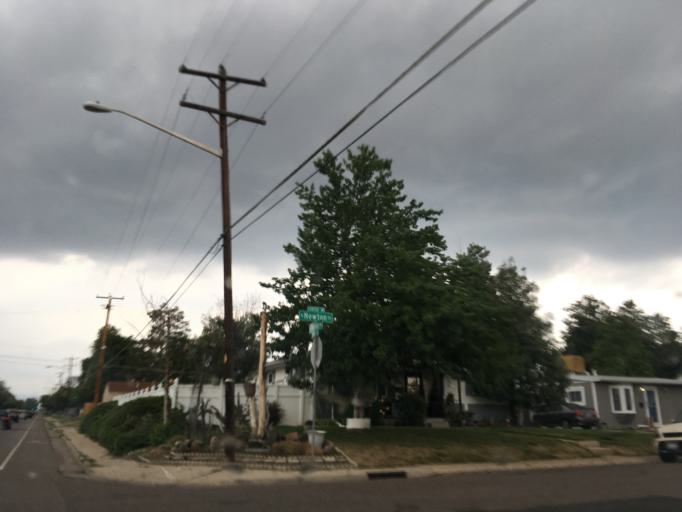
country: US
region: Colorado
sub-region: Arapahoe County
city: Sheridan
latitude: 39.6895
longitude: -105.0365
